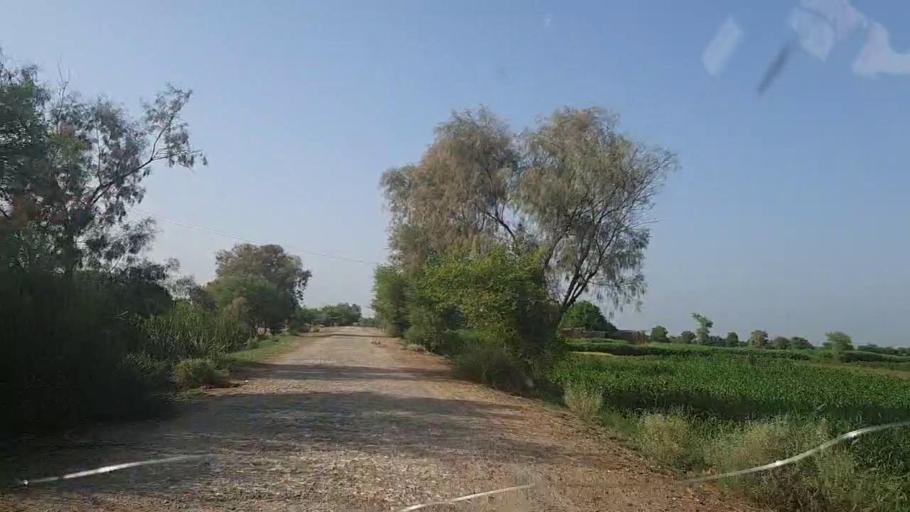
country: PK
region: Sindh
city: Khanpur
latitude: 27.7148
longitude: 69.3319
